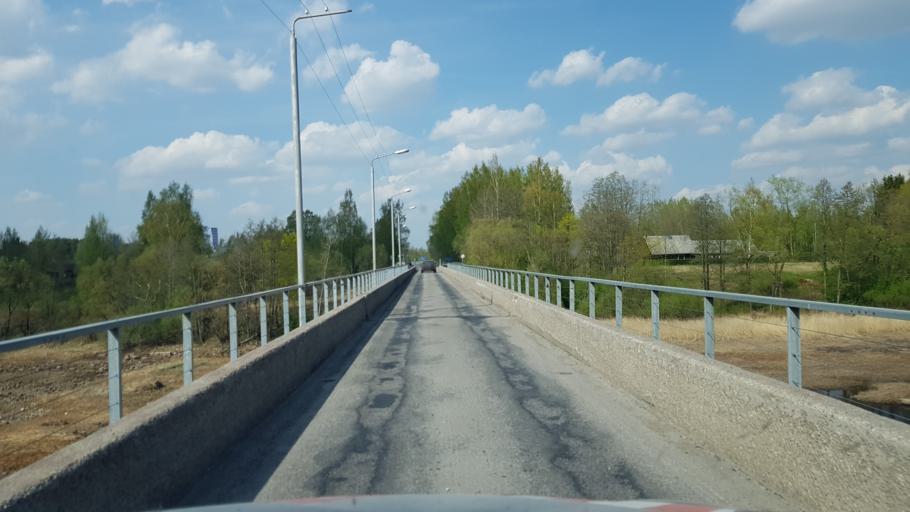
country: EE
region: Paernumaa
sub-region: Sindi linn
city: Sindi
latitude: 58.4168
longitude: 24.6711
